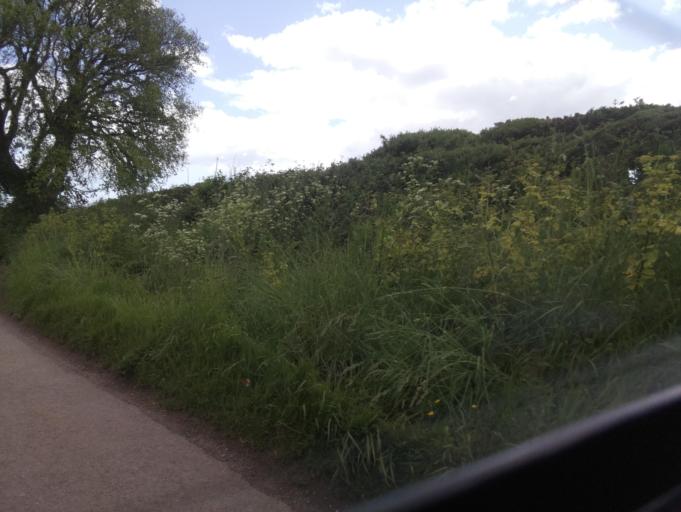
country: GB
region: England
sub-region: Devon
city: Dartmouth
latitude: 50.3610
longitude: -3.5482
